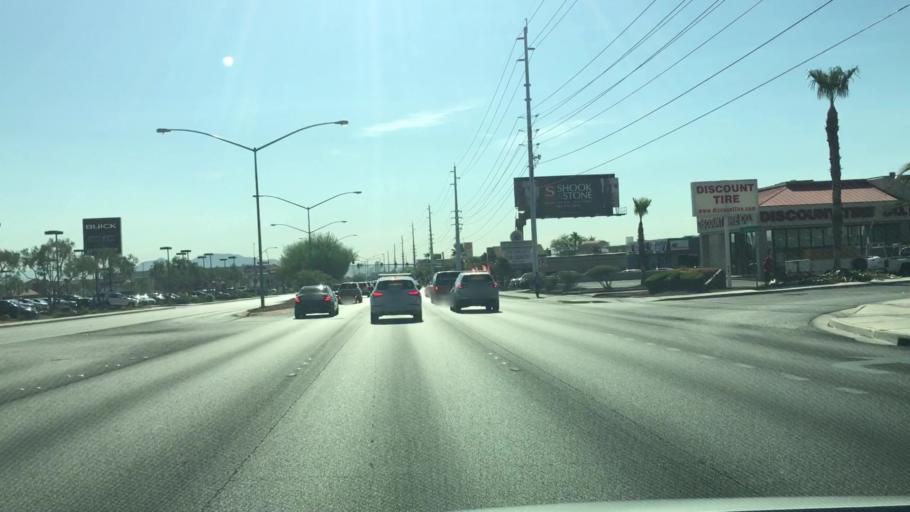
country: US
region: Nevada
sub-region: Clark County
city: Spring Valley
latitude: 36.1440
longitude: -115.2364
